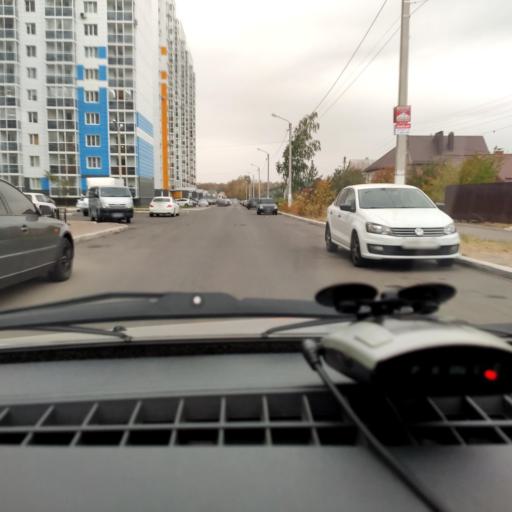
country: RU
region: Voronezj
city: Podgornoye
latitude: 51.7606
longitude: 39.1834
